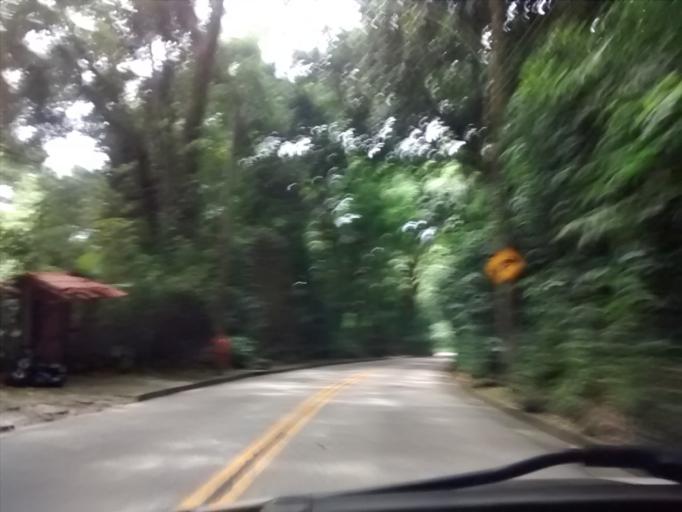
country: BR
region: Rio de Janeiro
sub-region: Rio De Janeiro
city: Rio de Janeiro
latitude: -22.9889
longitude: -43.2741
